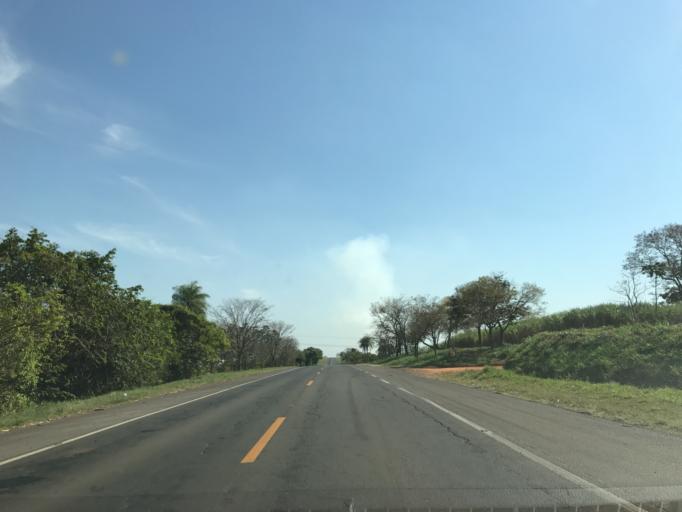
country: BR
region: Sao Paulo
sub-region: Penapolis
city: Penapolis
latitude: -21.3487
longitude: -50.0550
